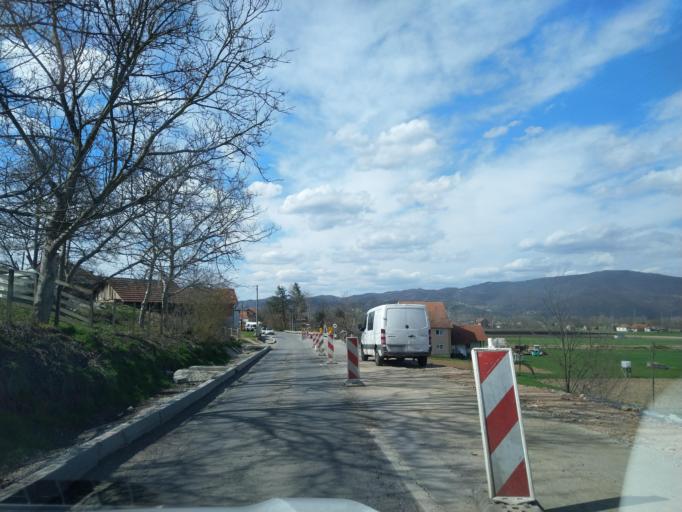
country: RS
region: Central Serbia
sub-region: Zlatiborski Okrug
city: Pozega
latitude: 43.8245
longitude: 20.0810
